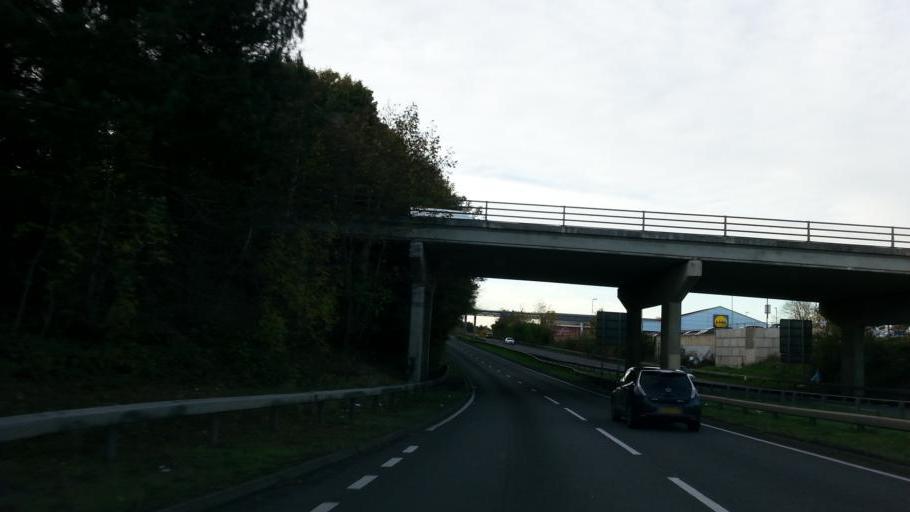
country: GB
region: England
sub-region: Northamptonshire
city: Northampton
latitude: 52.2540
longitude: -0.8354
